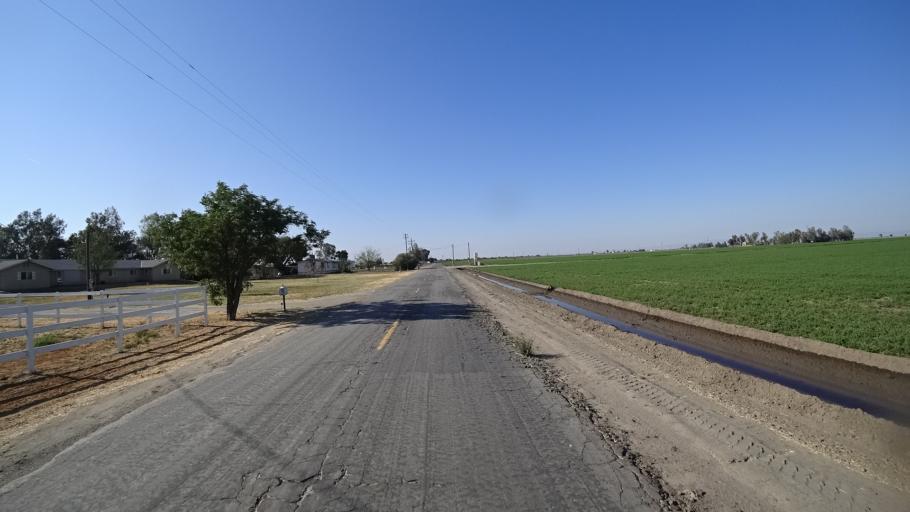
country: US
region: California
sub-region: Kings County
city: Lemoore Station
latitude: 36.3332
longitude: -119.8783
